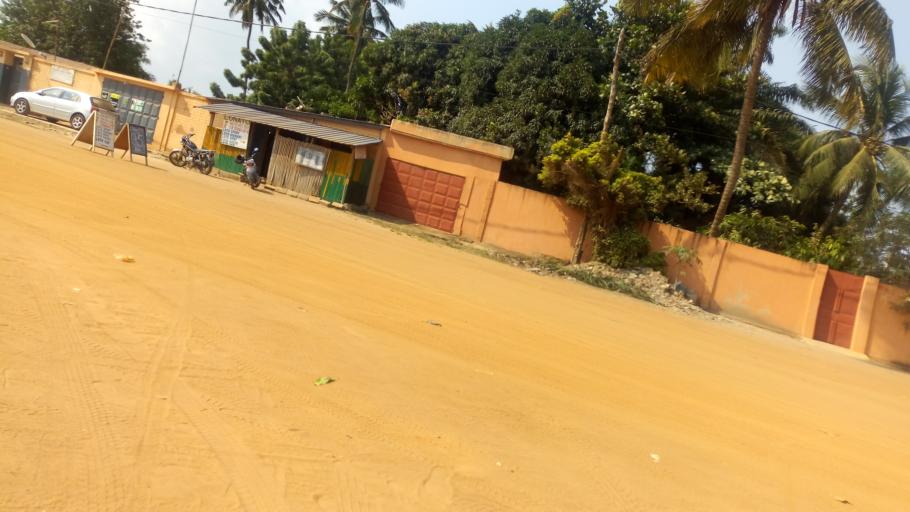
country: TG
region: Maritime
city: Lome
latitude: 6.1908
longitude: 1.1829
